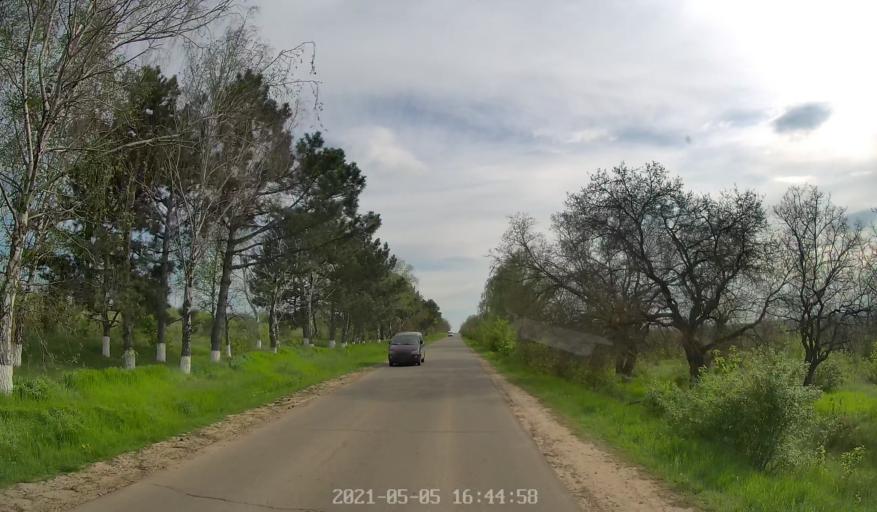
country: MD
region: Criuleni
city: Criuleni
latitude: 47.1138
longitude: 29.1942
